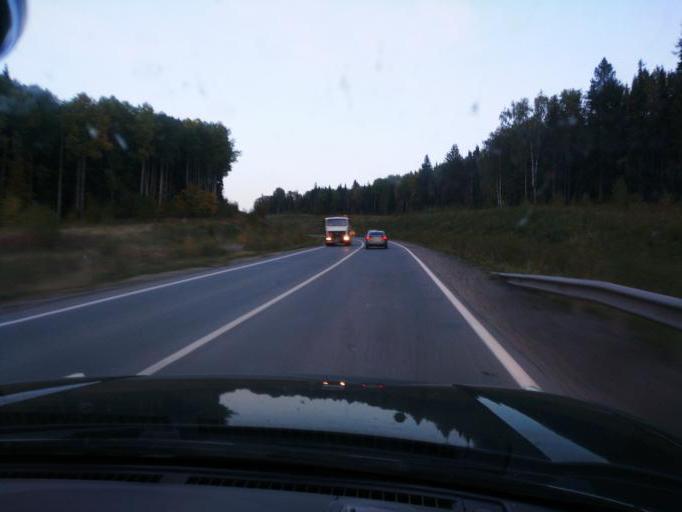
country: RU
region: Perm
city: Sylva
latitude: 58.2966
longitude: 56.8023
